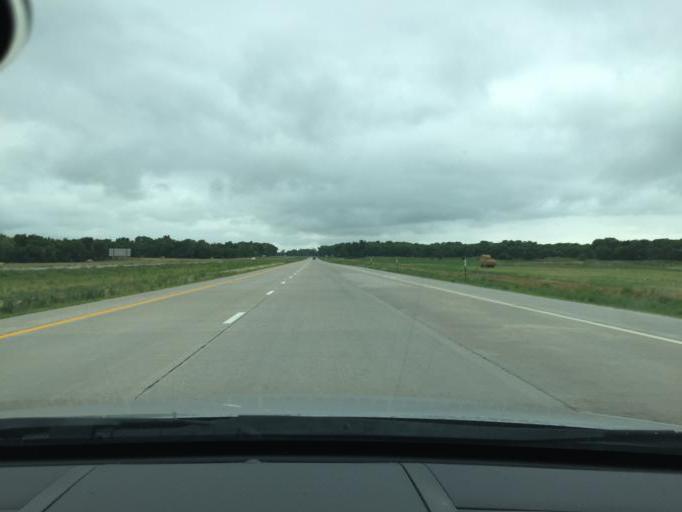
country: US
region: Kansas
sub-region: Reno County
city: Buhler
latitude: 38.1519
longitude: -97.8527
